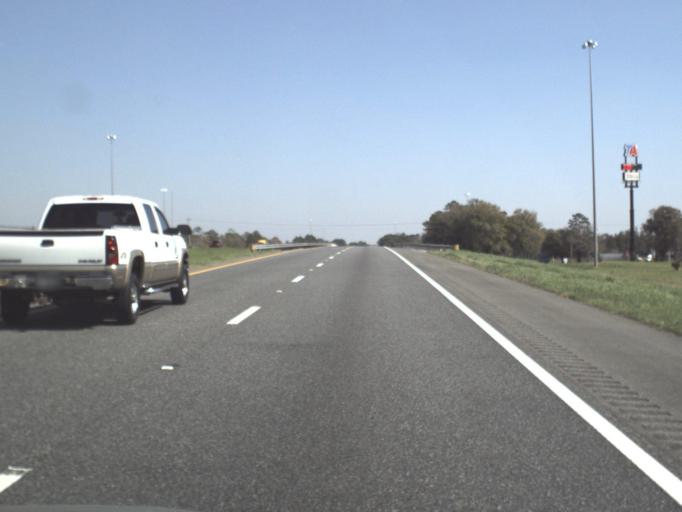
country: US
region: Florida
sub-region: Jackson County
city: Marianna
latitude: 30.7217
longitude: -85.1878
